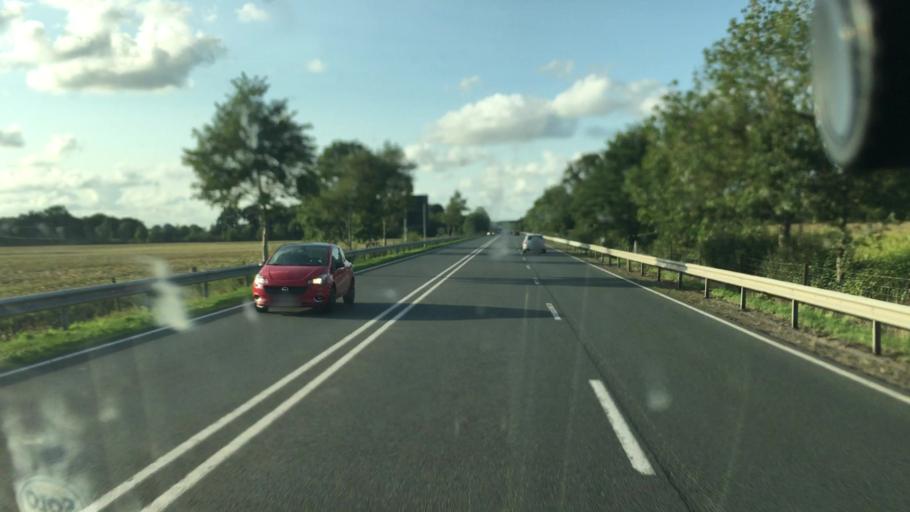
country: DE
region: Lower Saxony
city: Schortens
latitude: 53.5662
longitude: 7.9376
